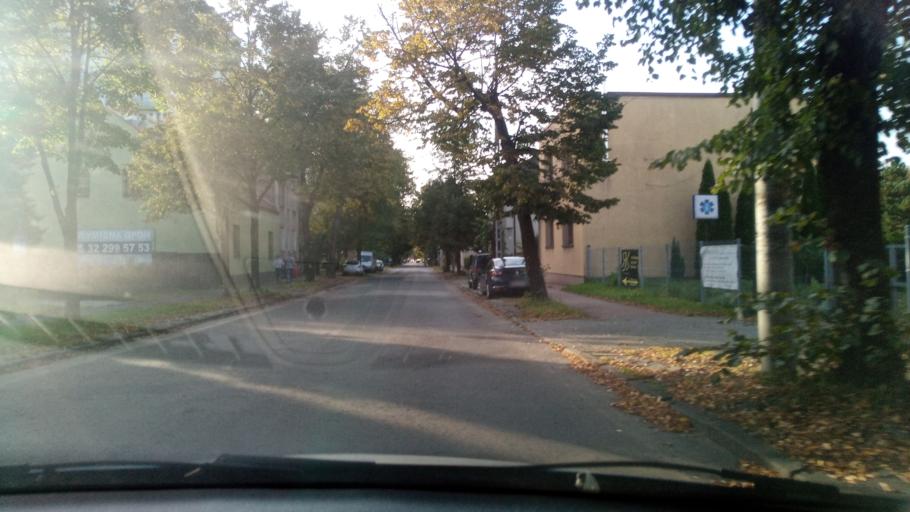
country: PL
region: Silesian Voivodeship
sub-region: Sosnowiec
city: Sosnowiec
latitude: 50.2825
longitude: 19.1123
